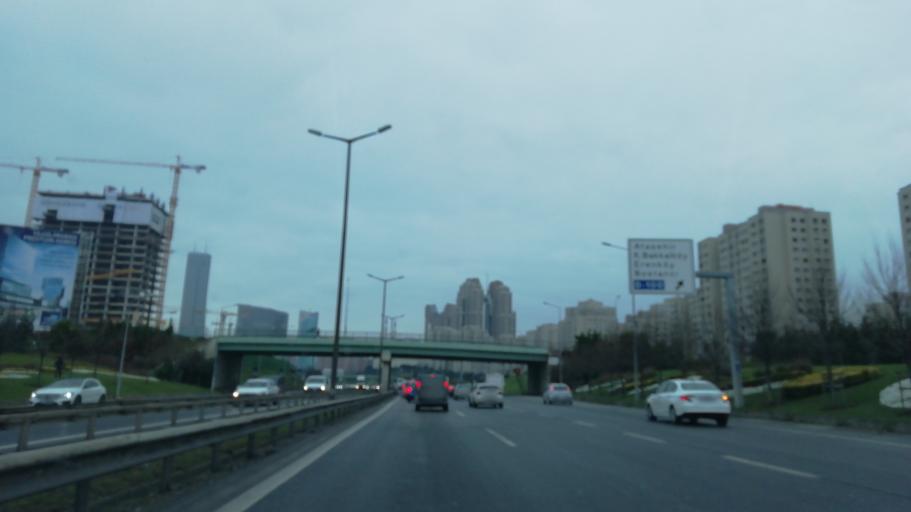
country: TR
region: Istanbul
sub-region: Atasehir
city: Atasehir
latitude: 41.0013
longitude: 29.1052
